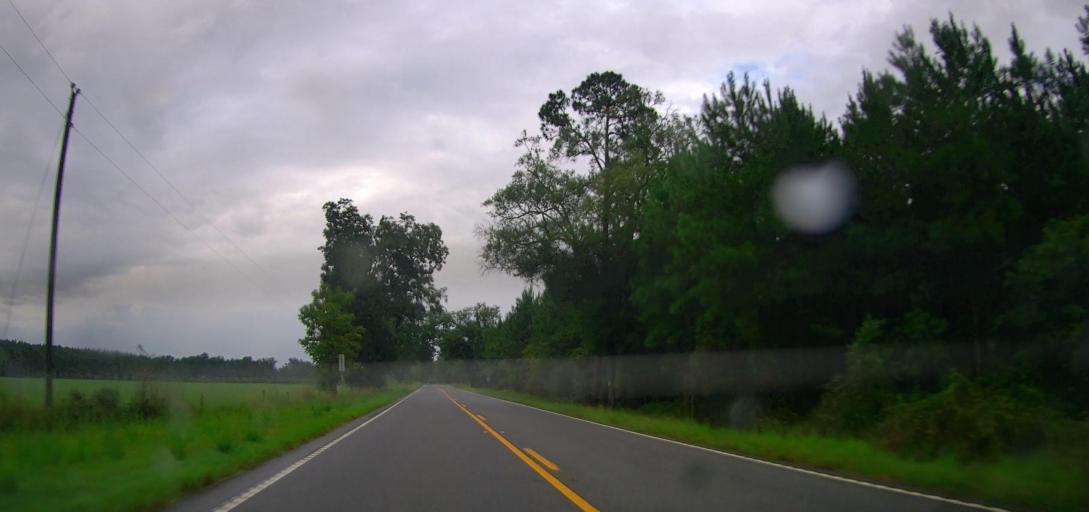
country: US
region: Georgia
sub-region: Ware County
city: Deenwood
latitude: 31.2723
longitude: -82.4122
